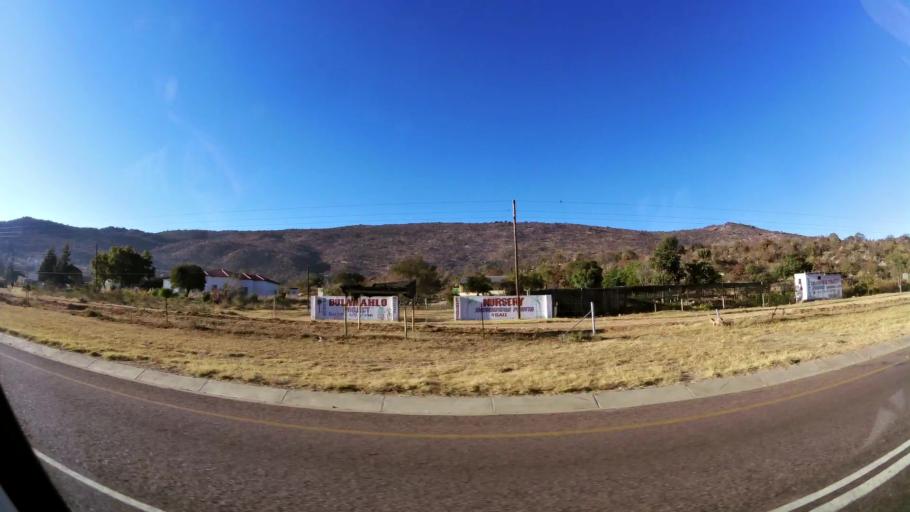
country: ZA
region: Limpopo
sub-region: Capricorn District Municipality
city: Mankoeng
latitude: -23.9417
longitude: 29.8235
